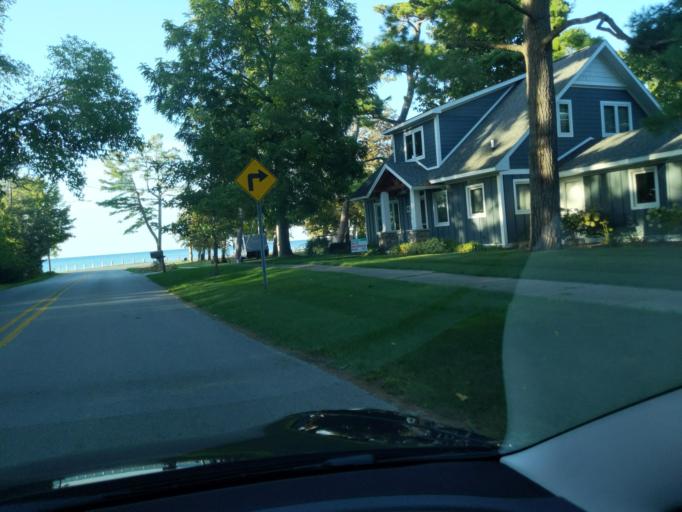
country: US
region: Michigan
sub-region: Antrim County
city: Elk Rapids
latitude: 44.8957
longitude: -85.4214
